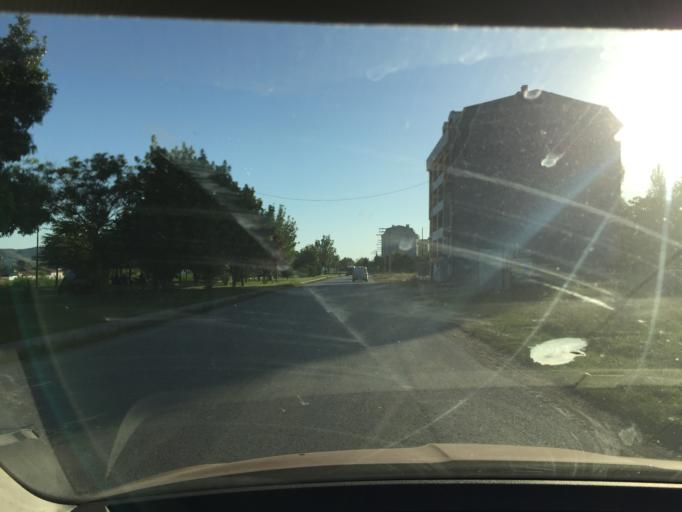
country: TR
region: Eskisehir
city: Eskisehir
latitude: 39.7749
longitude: 30.4535
